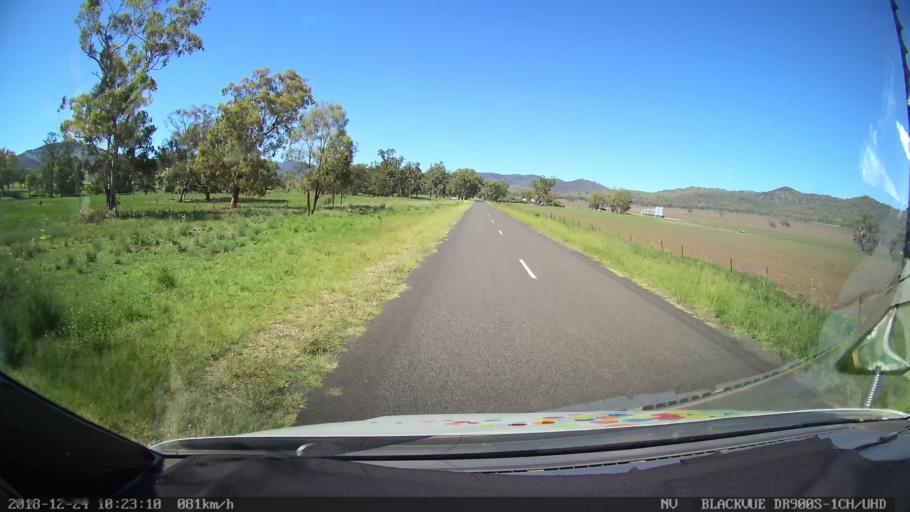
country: AU
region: New South Wales
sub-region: Liverpool Plains
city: Quirindi
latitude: -31.7722
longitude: 150.5399
